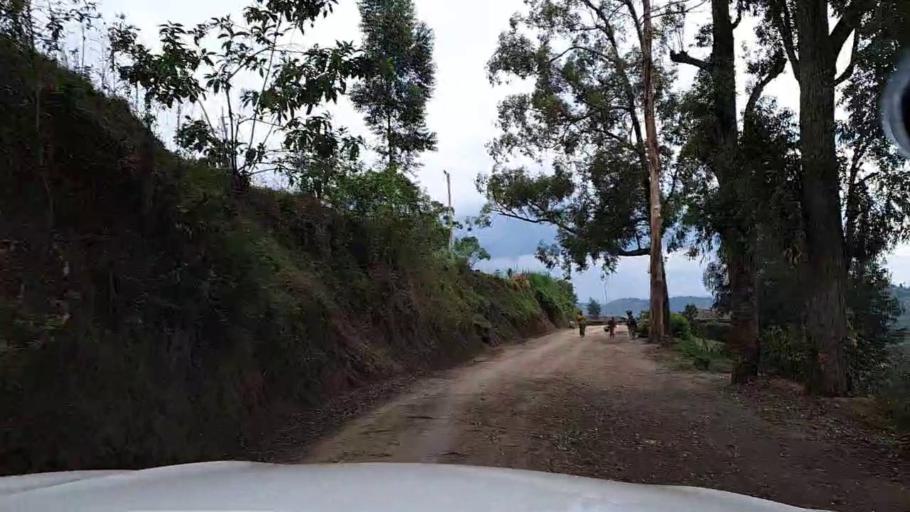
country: BI
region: Kayanza
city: Kayanza
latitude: -2.7967
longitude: 29.5078
